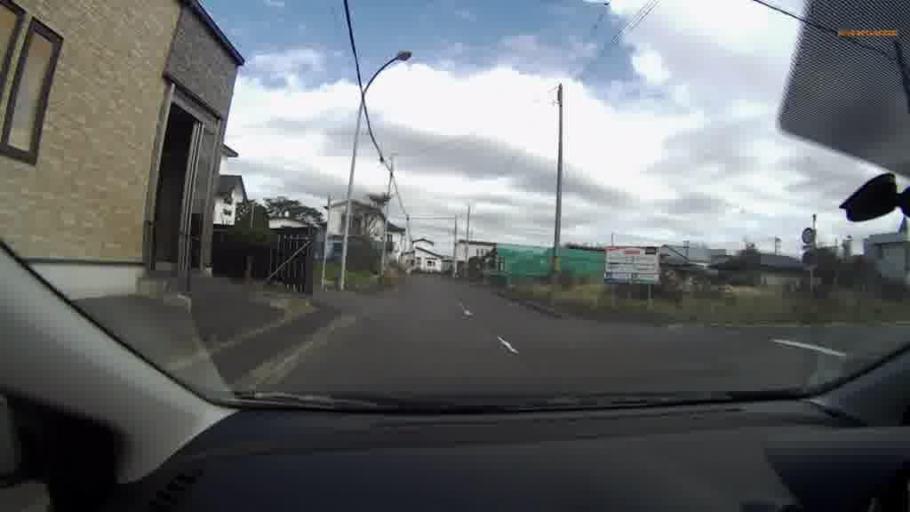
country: JP
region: Hokkaido
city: Kushiro
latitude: 43.0103
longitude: 144.2744
